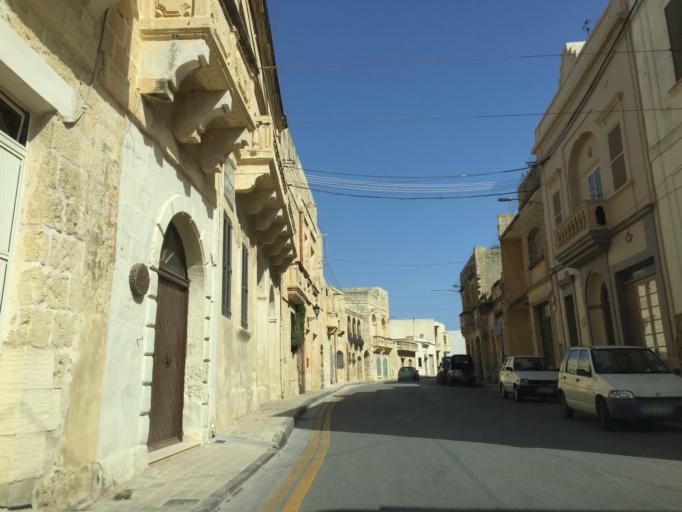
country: MT
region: L-Gharb
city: Gharb
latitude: 36.0587
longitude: 14.2102
